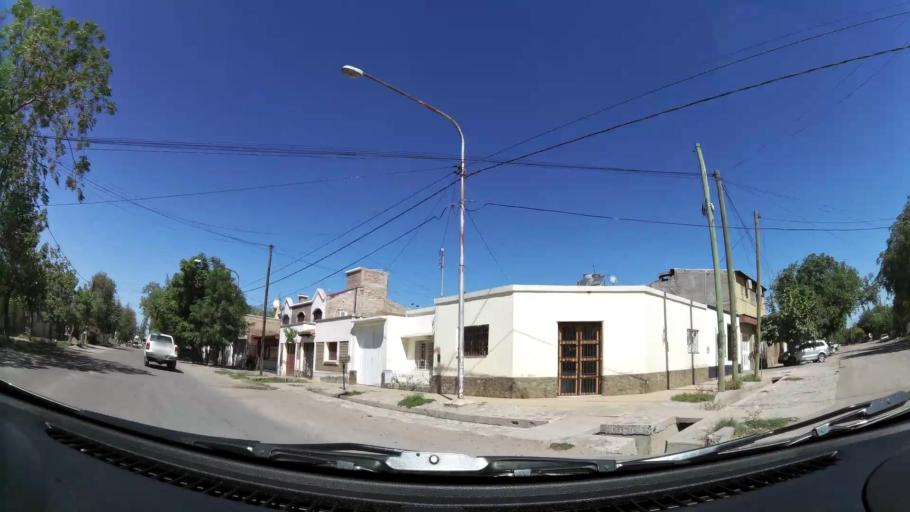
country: AR
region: Mendoza
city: Villa Nueva
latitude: -32.8933
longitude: -68.8028
